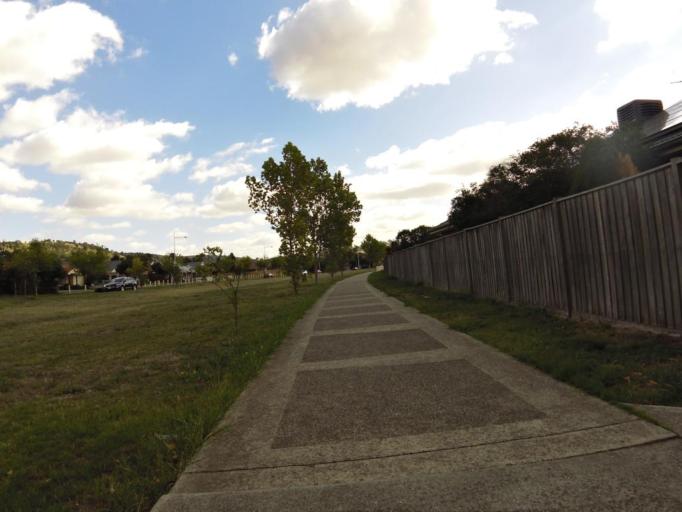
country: AU
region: Victoria
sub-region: Whittlesea
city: Mill Park
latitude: -37.6334
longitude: 145.0664
